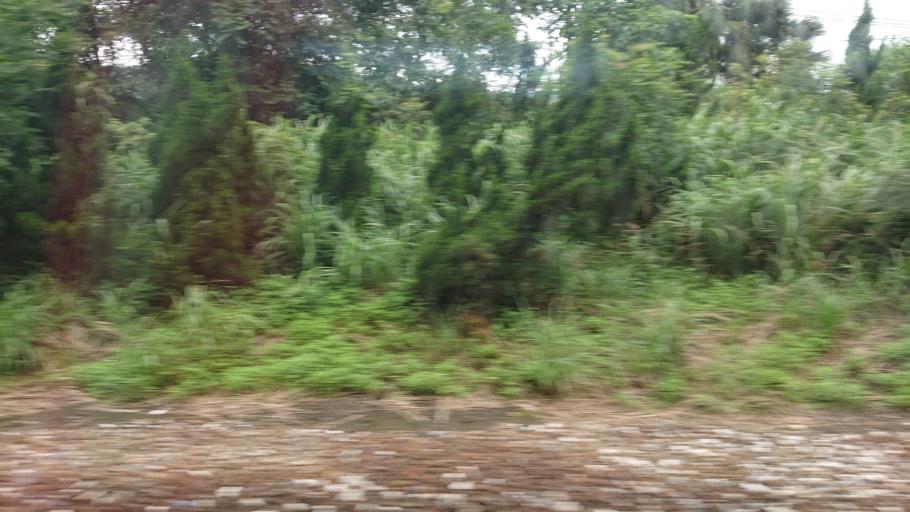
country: TW
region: Taiwan
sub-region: Keelung
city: Keelung
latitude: 25.1087
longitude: 121.8174
